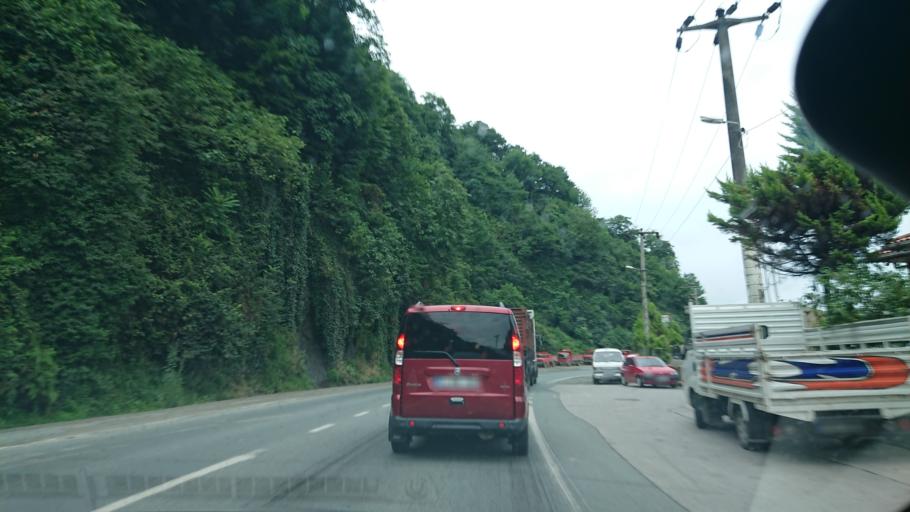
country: TR
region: Rize
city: Gundogdu
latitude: 41.0354
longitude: 40.5791
